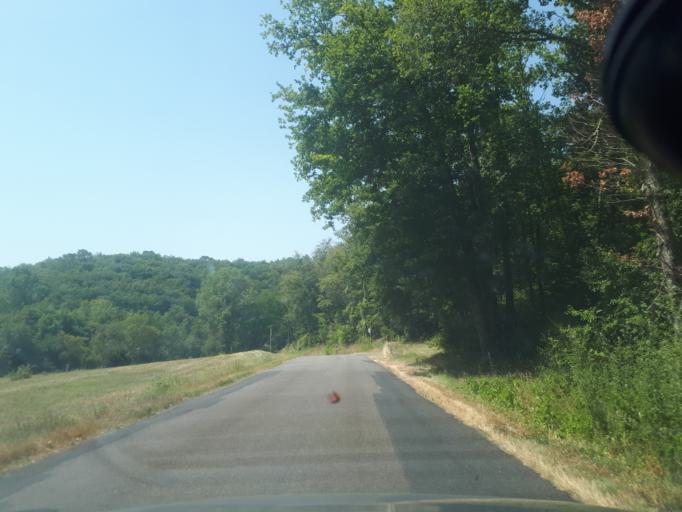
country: FR
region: Midi-Pyrenees
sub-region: Departement du Lot
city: Gourdon
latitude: 44.7857
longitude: 1.3641
